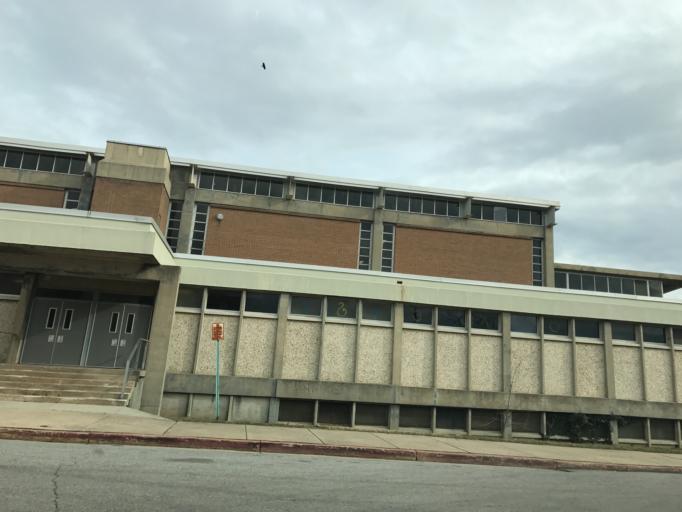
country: US
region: Maryland
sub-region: City of Baltimore
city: Baltimore
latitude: 39.3177
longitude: -76.5858
